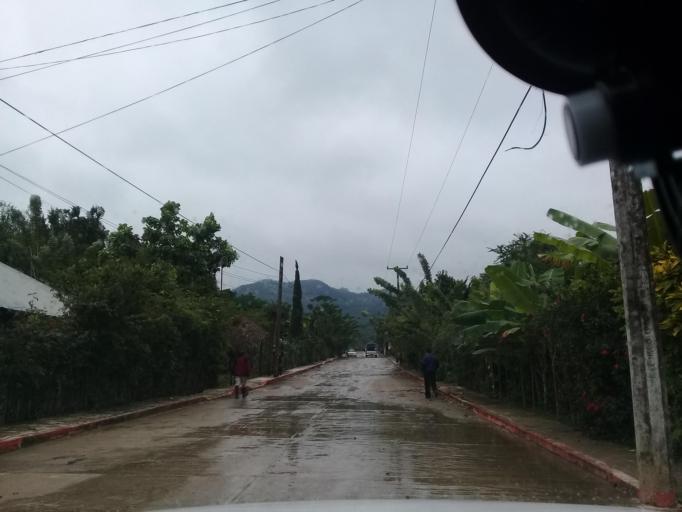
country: MX
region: Veracruz
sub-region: Chalma
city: San Pedro Coyutla
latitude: 21.2265
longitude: -98.4266
